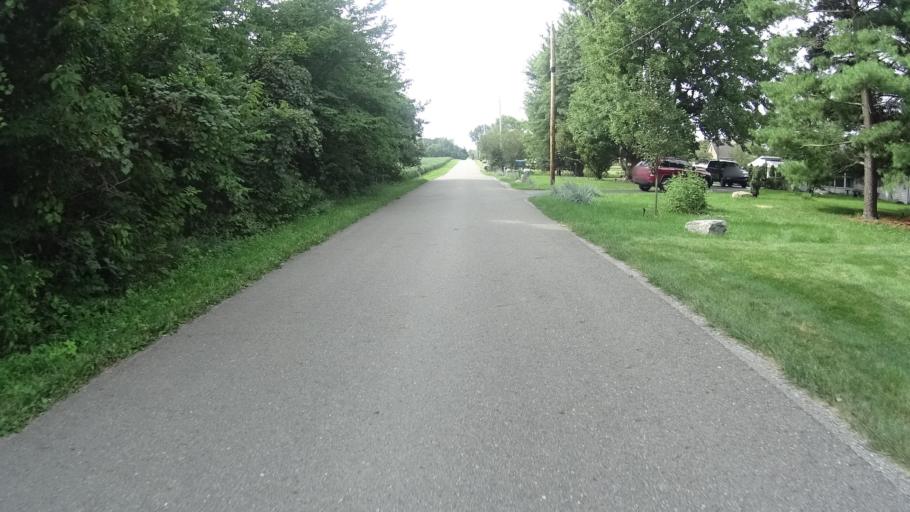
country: US
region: Indiana
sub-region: Madison County
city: Pendleton
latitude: 40.0029
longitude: -85.7870
